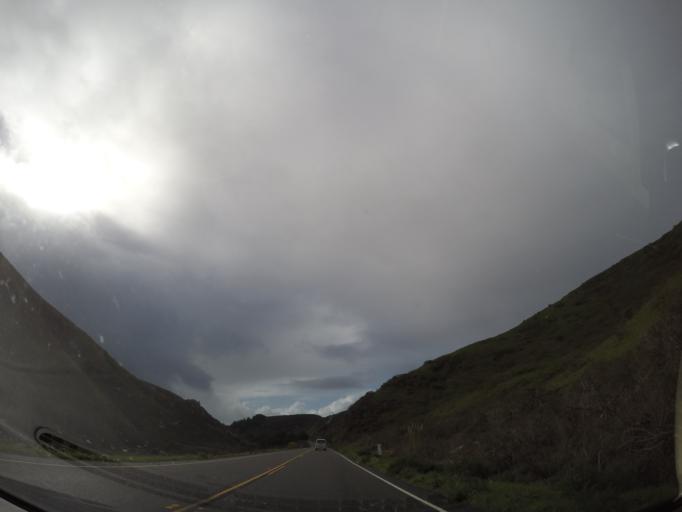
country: US
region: California
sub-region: Sonoma County
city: Bodega Bay
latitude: 38.3265
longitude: -123.0080
